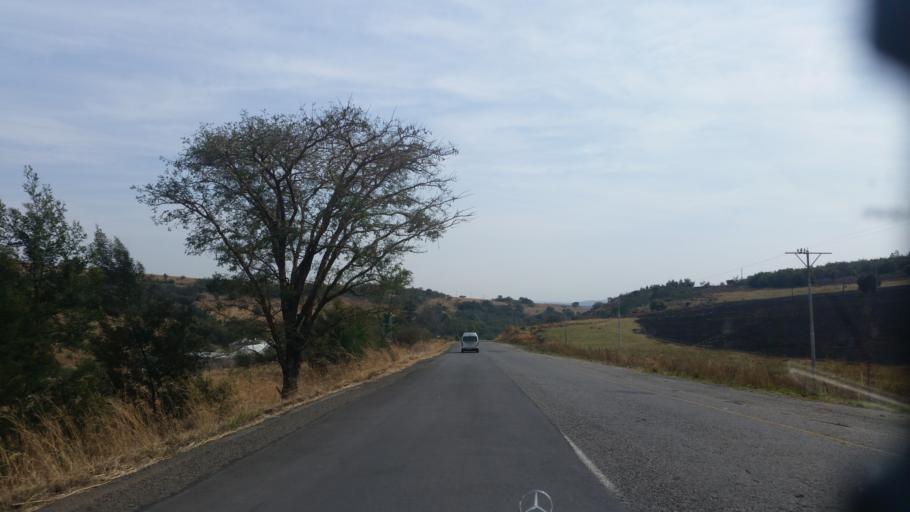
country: ZA
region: KwaZulu-Natal
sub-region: uThukela District Municipality
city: Estcourt
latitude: -29.0823
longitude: 29.9598
